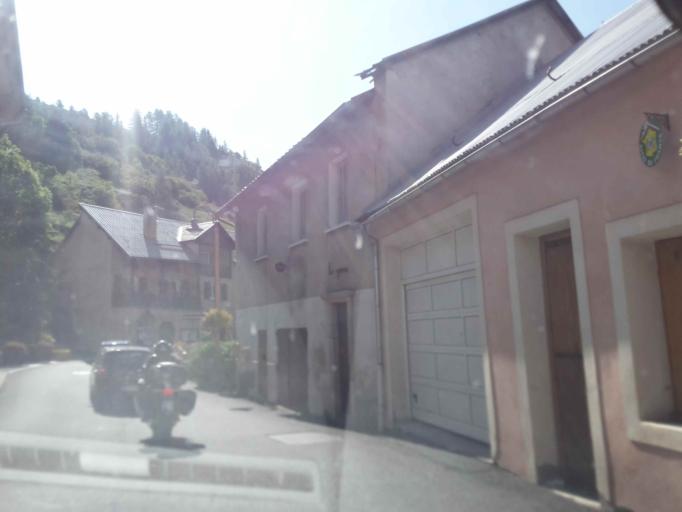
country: FR
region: Provence-Alpes-Cote d'Azur
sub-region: Departement des Hautes-Alpes
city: Guillestre
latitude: 44.6100
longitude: 6.6880
